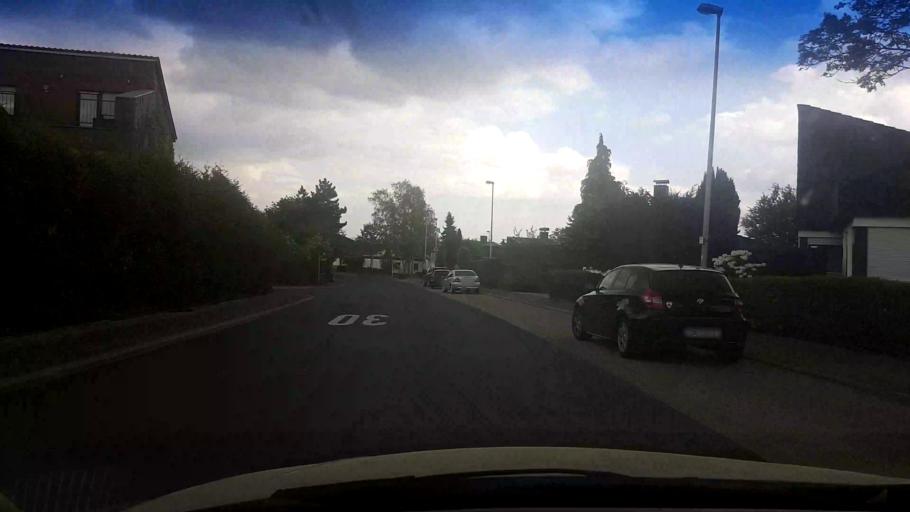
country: DE
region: Bavaria
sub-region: Upper Franconia
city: Stegaurach
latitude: 49.8727
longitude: 10.8736
